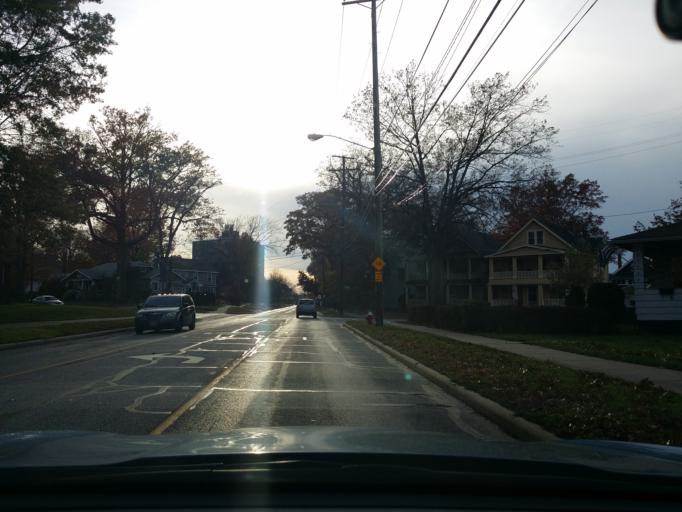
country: US
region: Ohio
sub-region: Cuyahoga County
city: Lakewood
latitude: 41.4803
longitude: -81.8033
